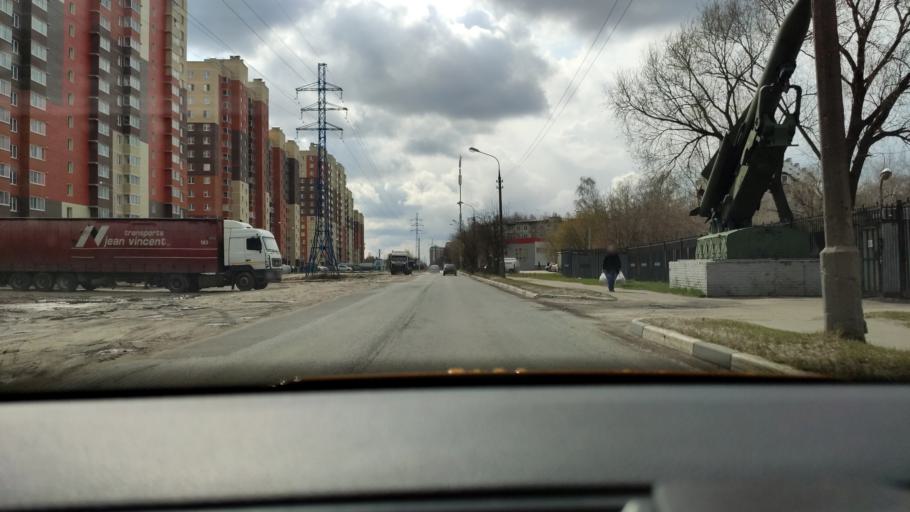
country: RU
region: Moskovskaya
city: Zheleznodorozhnyy
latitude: 55.7424
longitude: 38.0323
